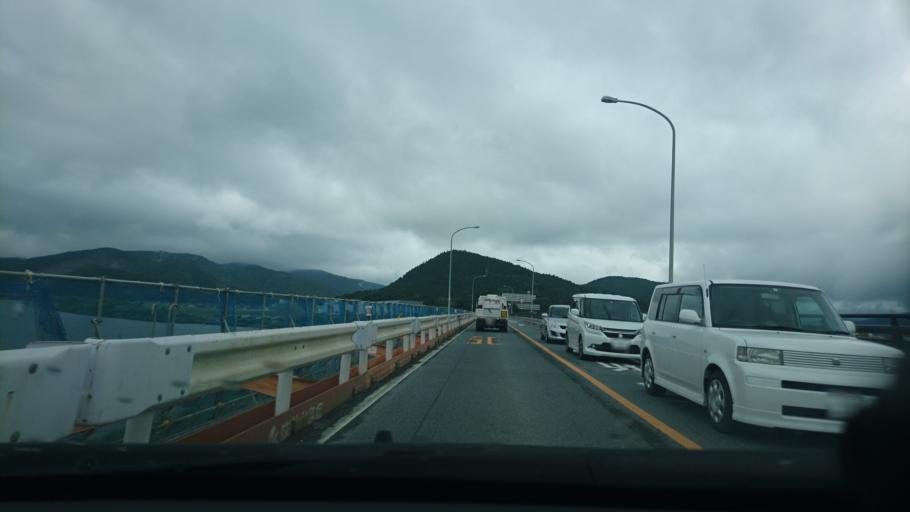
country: JP
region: Miyagi
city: Ishinomaki
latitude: 38.5126
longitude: 141.3061
